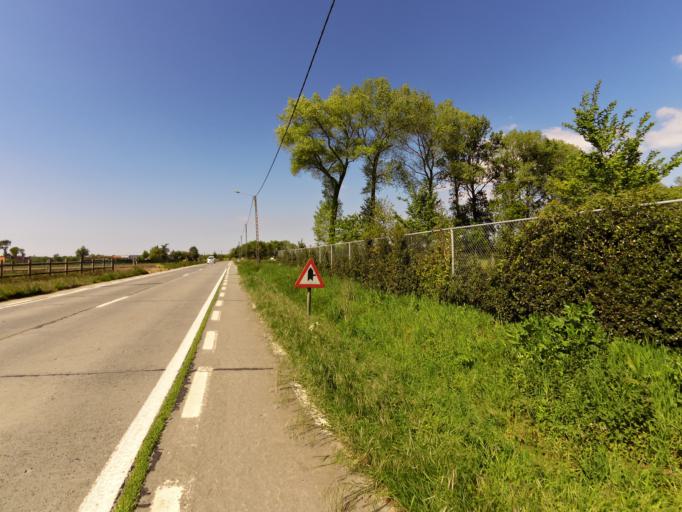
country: BE
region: Flanders
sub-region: Provincie West-Vlaanderen
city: Koekelare
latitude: 51.0624
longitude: 2.9386
